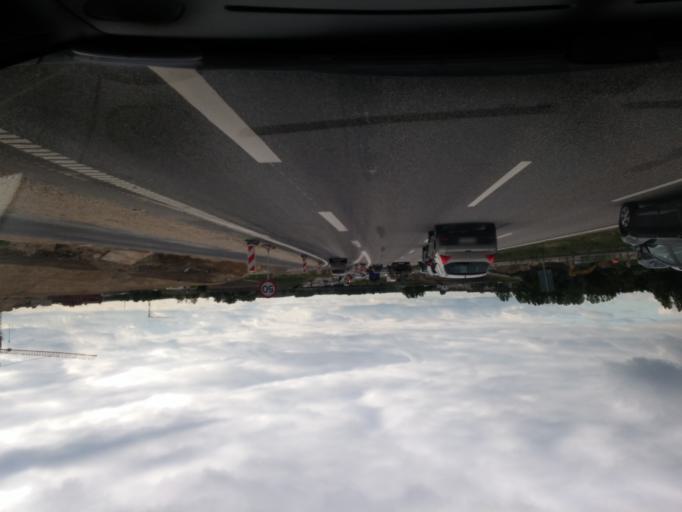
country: DK
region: Zealand
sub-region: Koge Kommune
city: Koge
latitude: 55.4888
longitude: 12.1676
